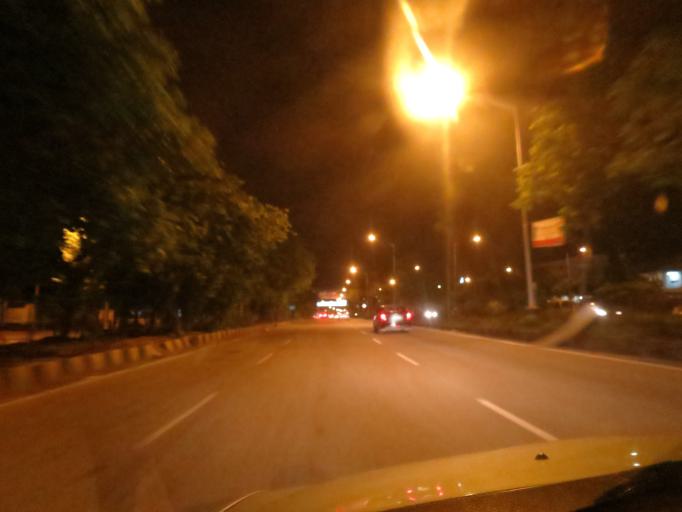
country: IN
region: Karnataka
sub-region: Bangalore Urban
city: Bangalore
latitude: 13.0260
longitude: 77.6388
